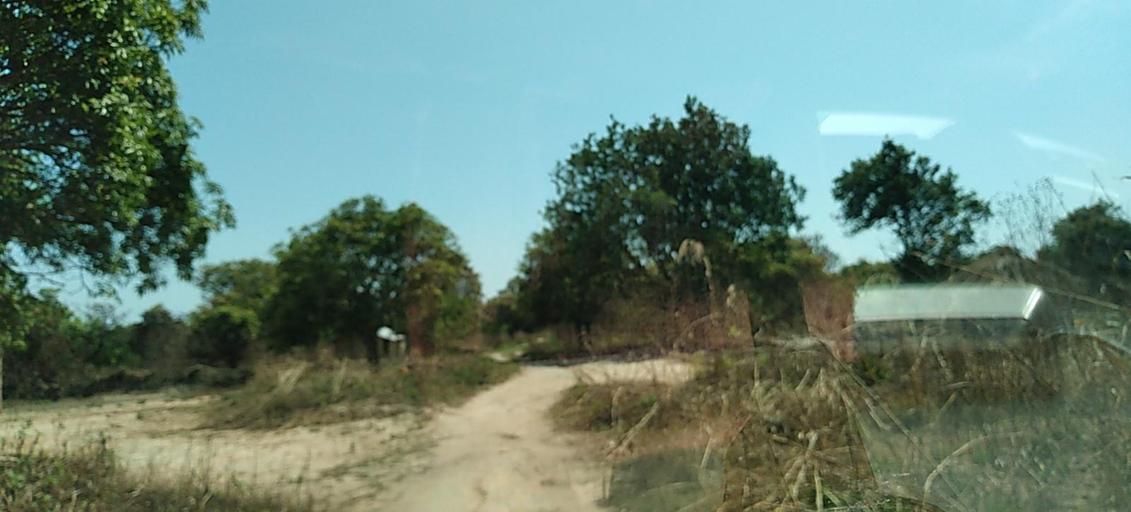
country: ZM
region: Copperbelt
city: Chililabombwe
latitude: -12.2868
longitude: 27.8803
